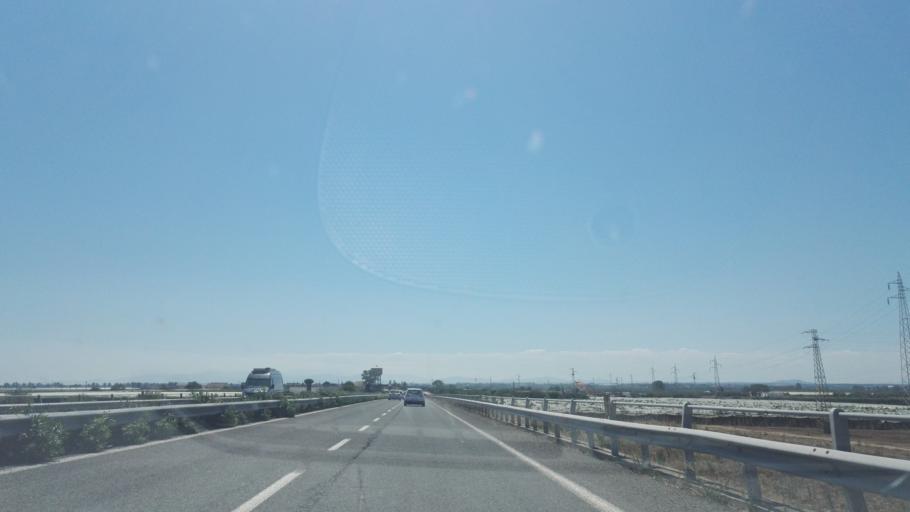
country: IT
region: Apulia
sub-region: Provincia di Taranto
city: Marina di Ginosa
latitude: 40.4416
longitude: 16.8472
